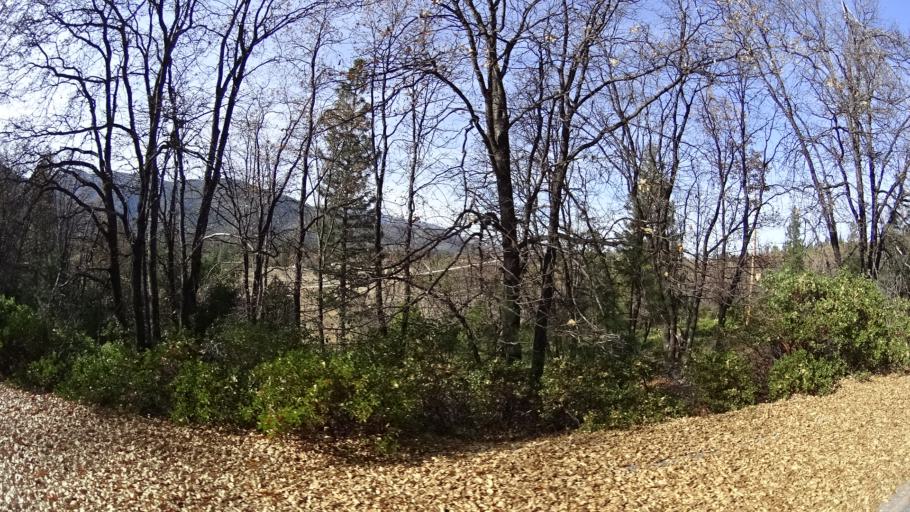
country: US
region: California
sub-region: Siskiyou County
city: Weed
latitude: 41.4023
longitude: -122.4173
